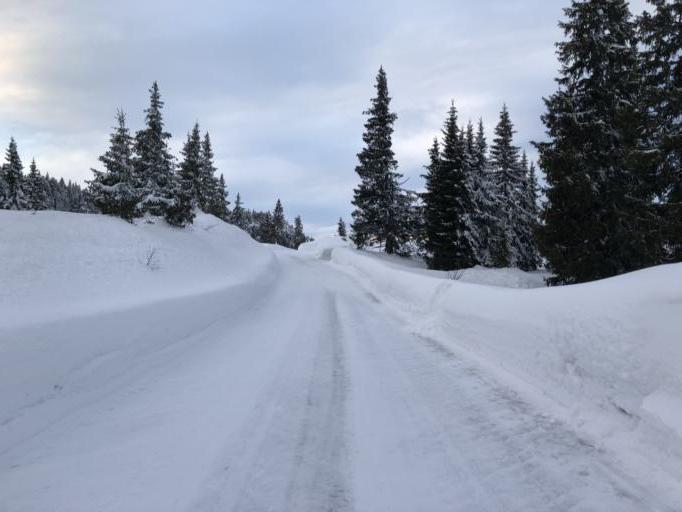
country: NO
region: Oppland
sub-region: Gausdal
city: Segalstad bru
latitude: 61.3311
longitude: 10.0519
